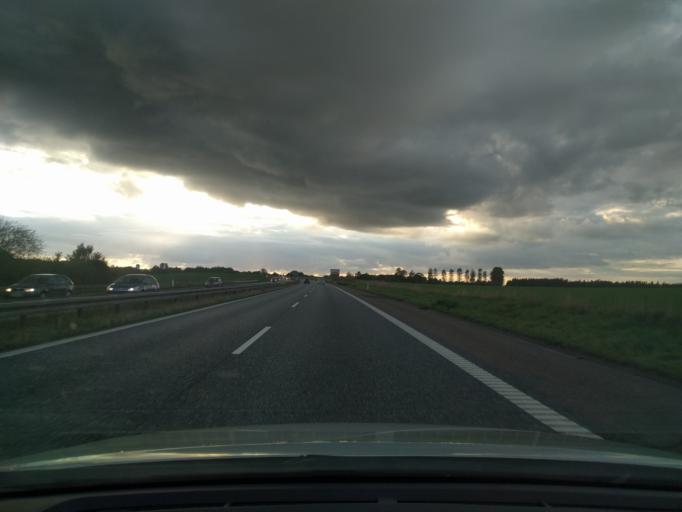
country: DK
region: Zealand
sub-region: Slagelse Kommune
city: Slagelse
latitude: 55.4290
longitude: 11.4408
